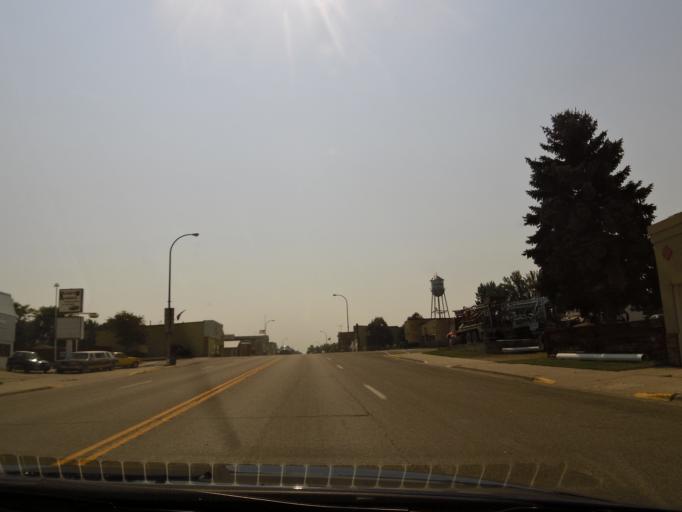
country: US
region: South Dakota
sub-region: Roberts County
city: Sisseton
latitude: 46.0772
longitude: -97.1520
